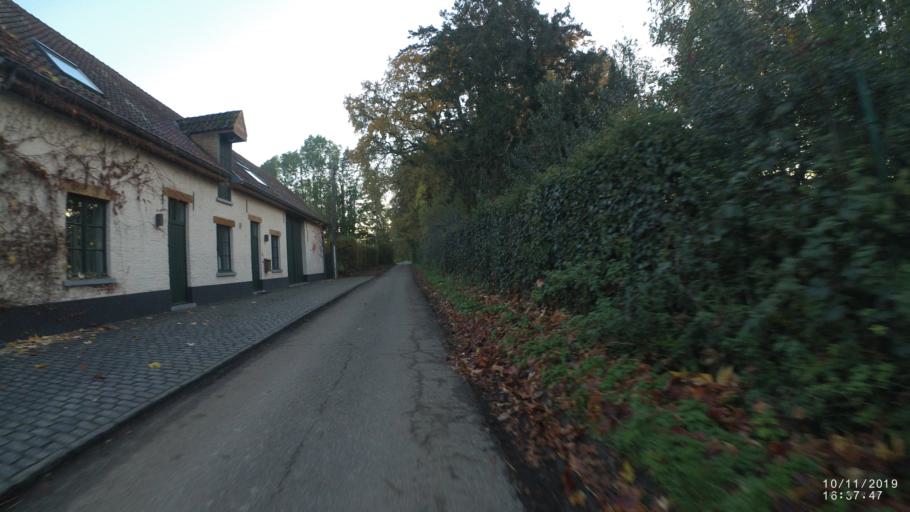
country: BE
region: Flanders
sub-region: Provincie Vlaams-Brabant
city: Bierbeek
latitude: 50.8664
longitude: 4.7755
